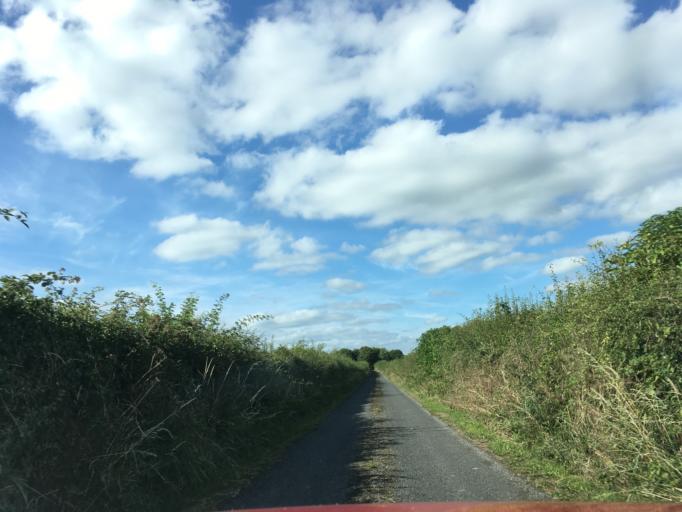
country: IE
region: Munster
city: Cashel
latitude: 52.4592
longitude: -7.9416
